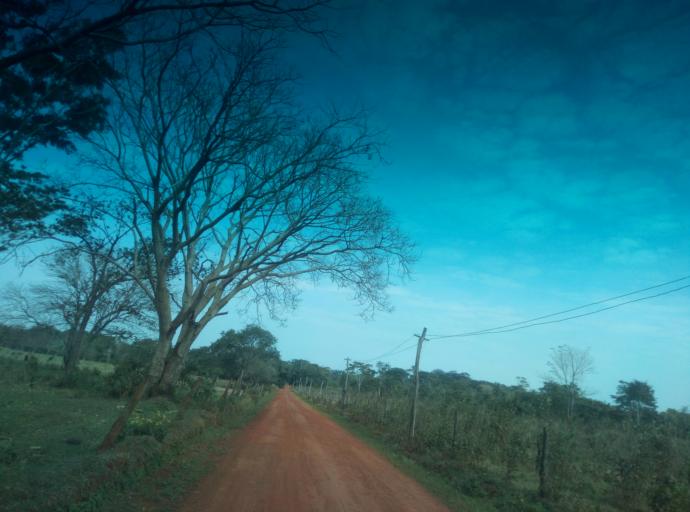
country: PY
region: Caaguazu
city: Carayao
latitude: -25.1982
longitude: -56.2529
